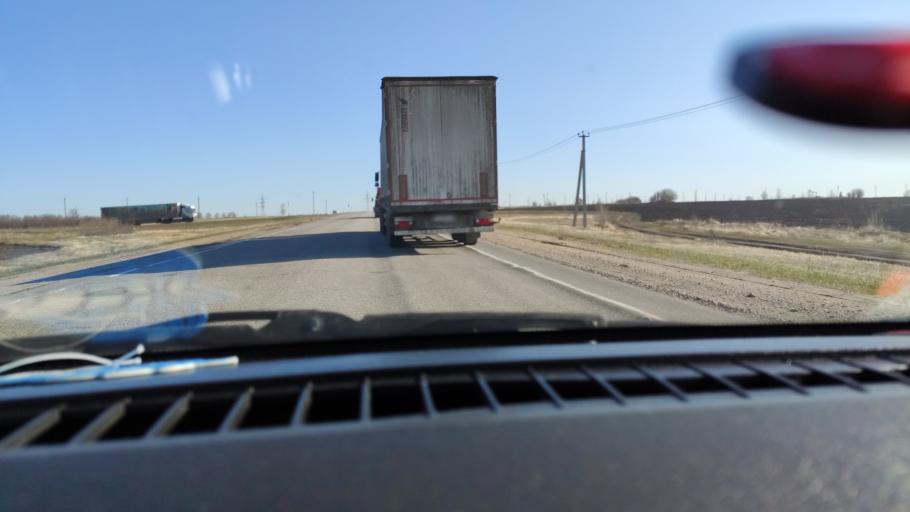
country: RU
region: Samara
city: Varlamovo
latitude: 53.1796
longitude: 48.2859
